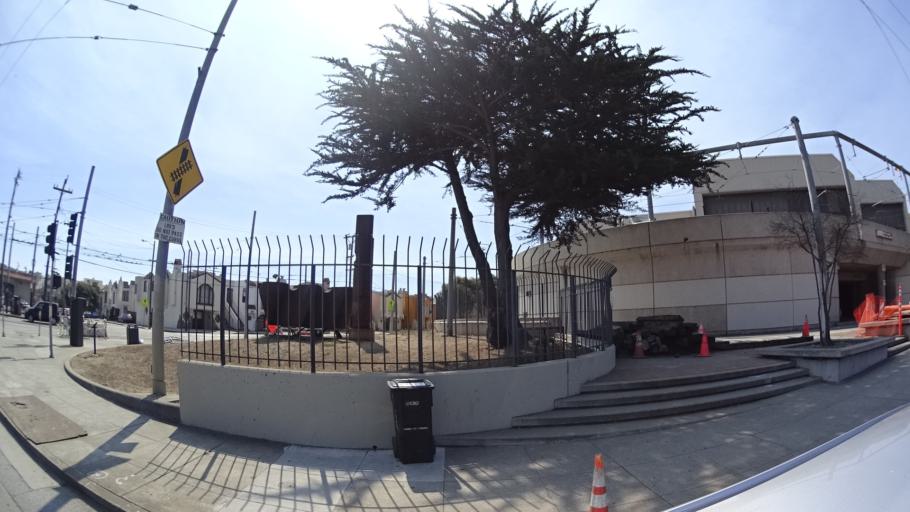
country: US
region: California
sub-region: San Mateo County
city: Daly City
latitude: 37.7229
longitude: -122.4453
